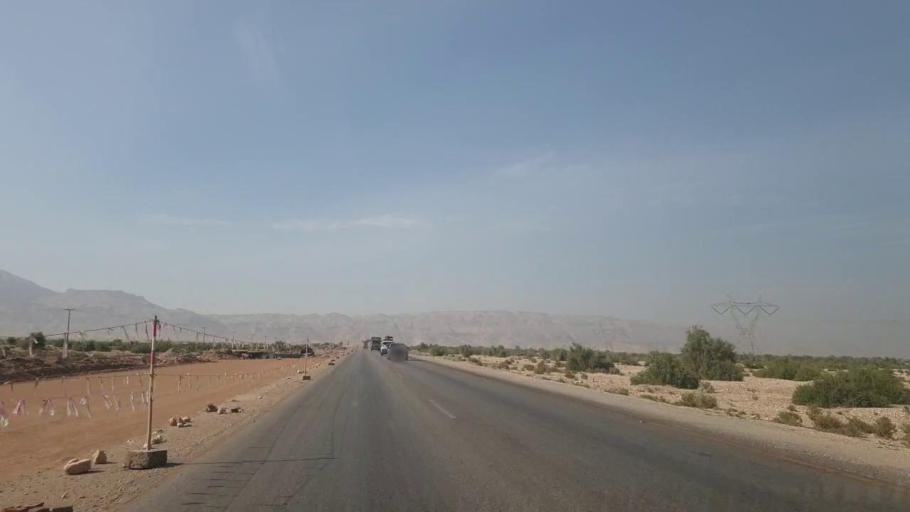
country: PK
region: Sindh
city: Sehwan
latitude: 26.2133
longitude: 67.9193
